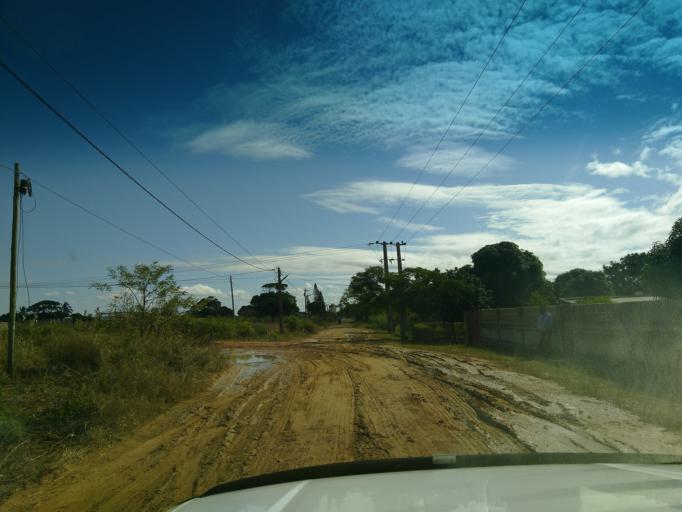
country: MZ
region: Maputo City
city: Maputo
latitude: -25.9945
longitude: 32.5368
